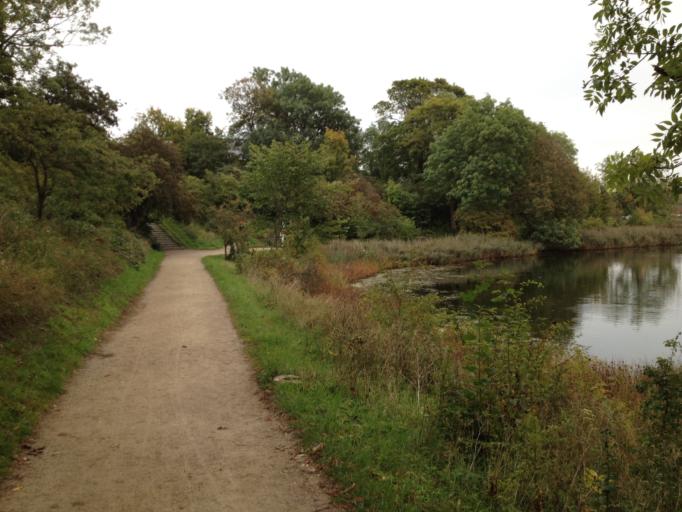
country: DK
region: Capital Region
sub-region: Kobenhavn
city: Christianshavn
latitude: 55.6697
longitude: 12.5874
